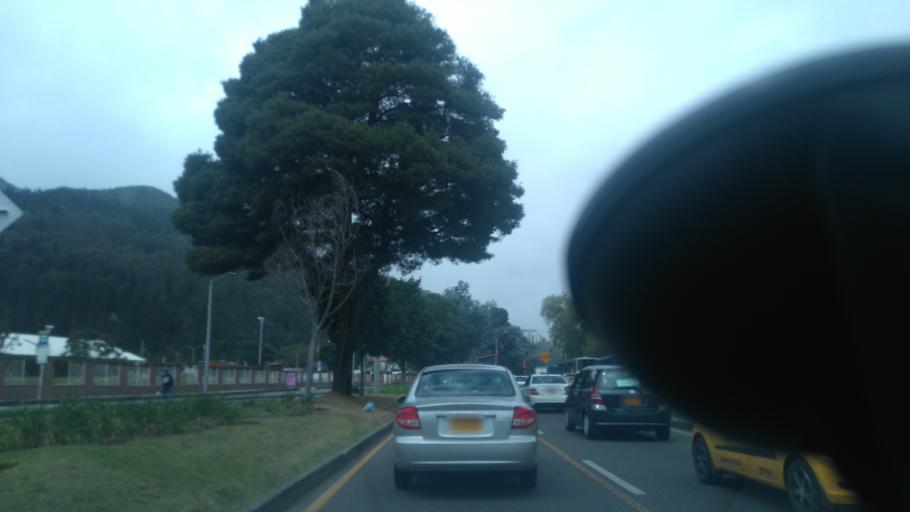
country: CO
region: Bogota D.C.
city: Barrio San Luis
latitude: 4.6865
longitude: -74.0353
